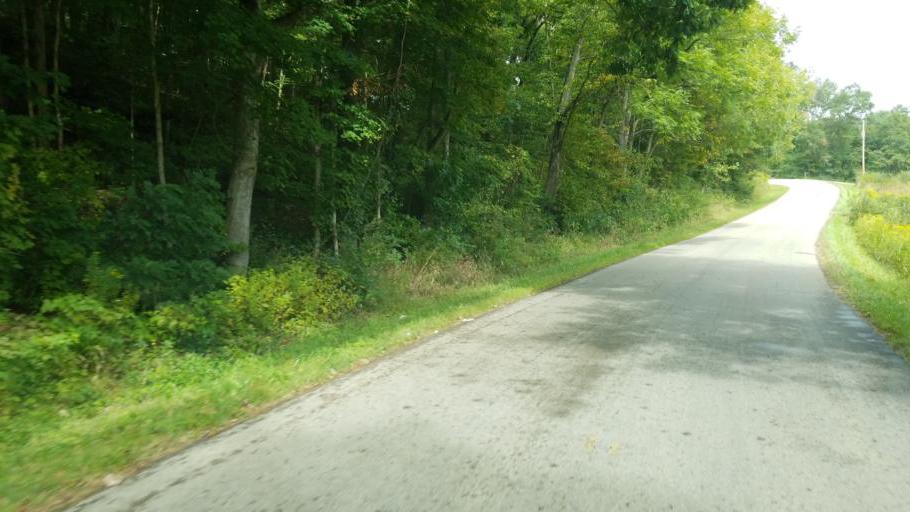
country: US
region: Ohio
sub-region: Jackson County
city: Oak Hill
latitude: 38.8878
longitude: -82.6070
